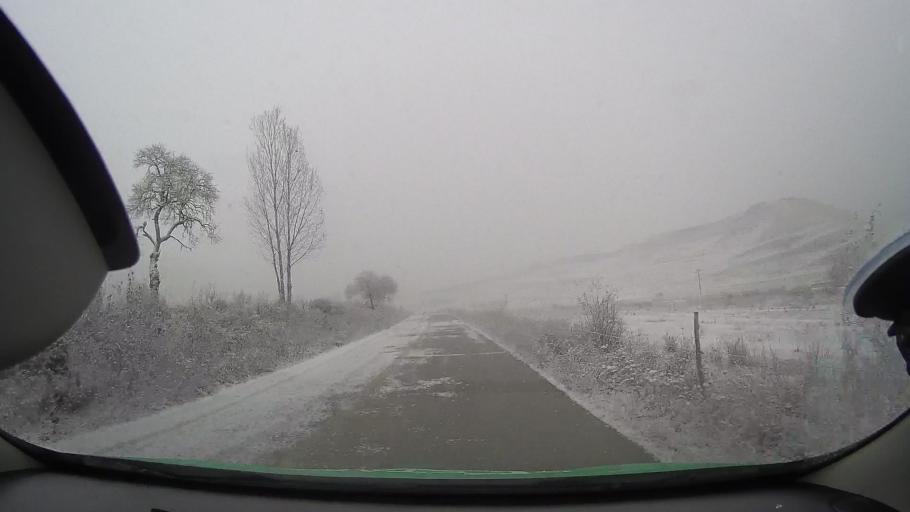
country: RO
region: Alba
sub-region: Comuna Hoparta
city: Hoparta
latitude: 46.3099
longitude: 23.8586
